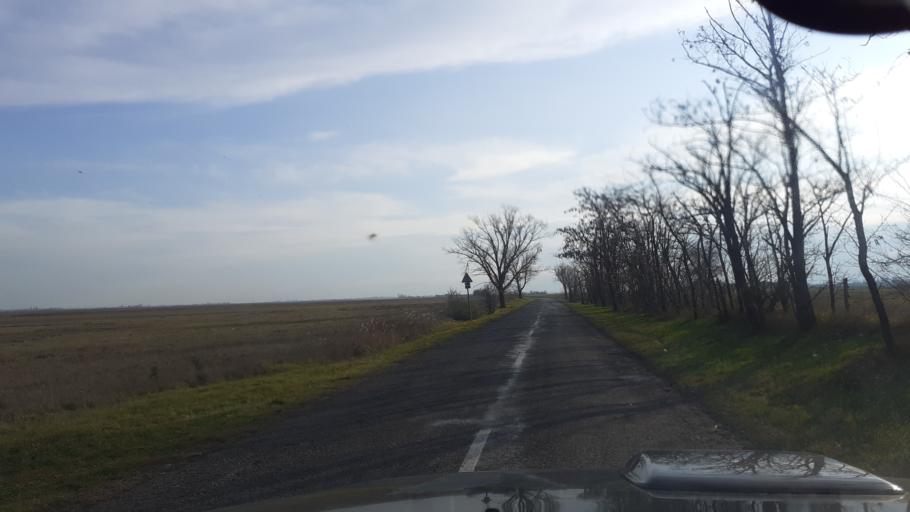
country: HU
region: Bacs-Kiskun
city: Kunszentmiklos
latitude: 47.0906
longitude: 19.0942
